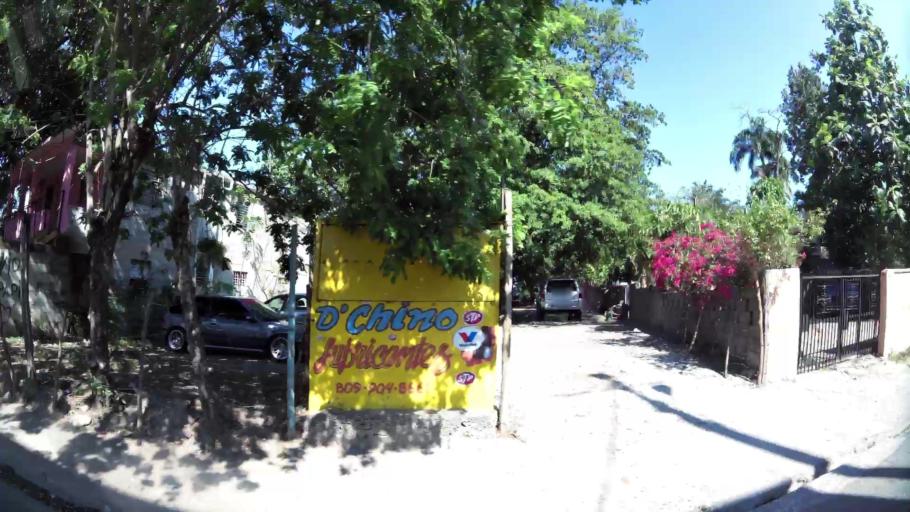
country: DO
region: Santo Domingo
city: Santo Domingo Oeste
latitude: 18.4676
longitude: -69.9987
